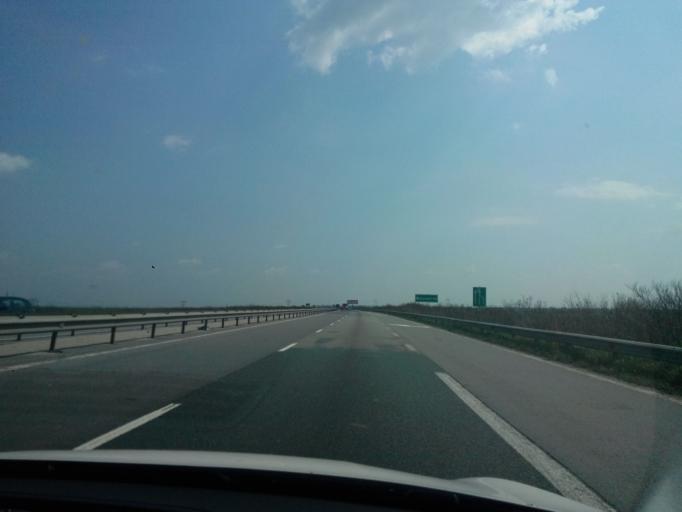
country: RO
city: Oarja Sat
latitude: 44.7846
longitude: 24.9955
